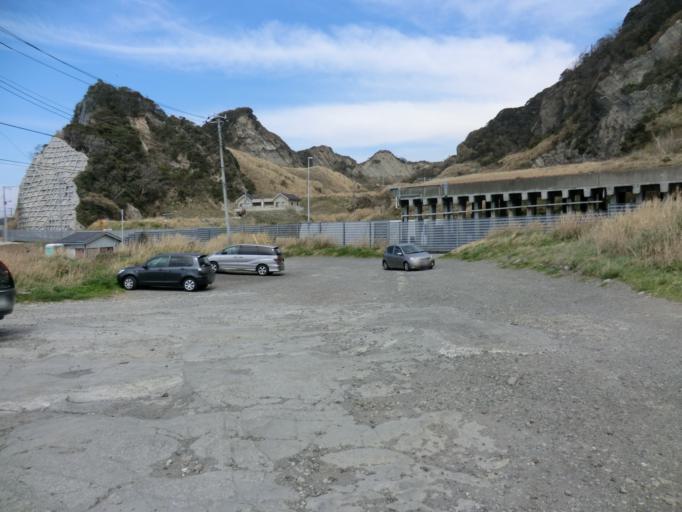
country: JP
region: Chiba
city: Futtsu
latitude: 35.1555
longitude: 139.8191
